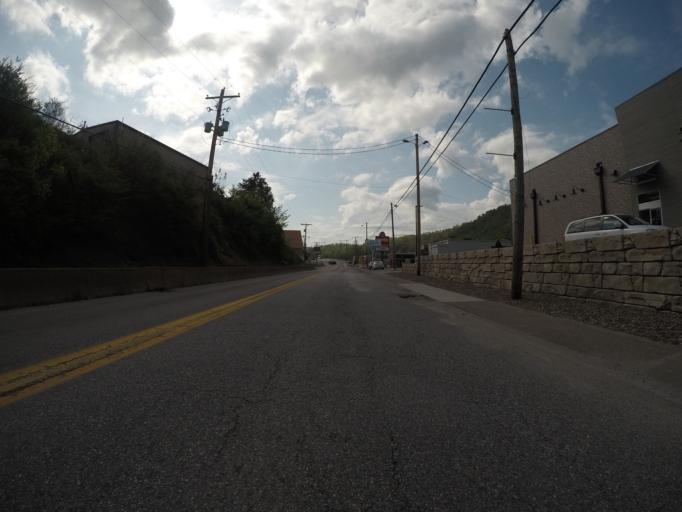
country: US
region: West Virginia
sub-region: Boone County
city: Madison
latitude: 38.0788
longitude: -81.8326
